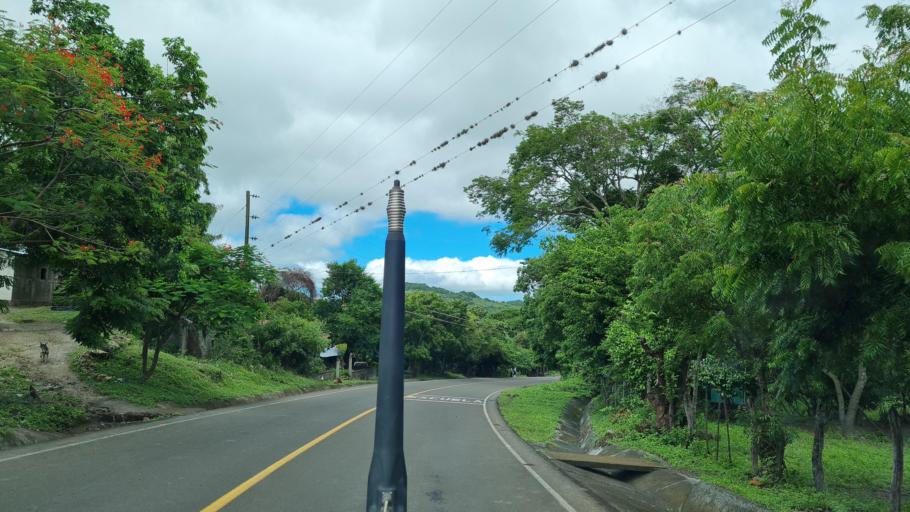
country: NI
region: Matagalpa
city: Terrabona
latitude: 12.5867
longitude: -85.9662
